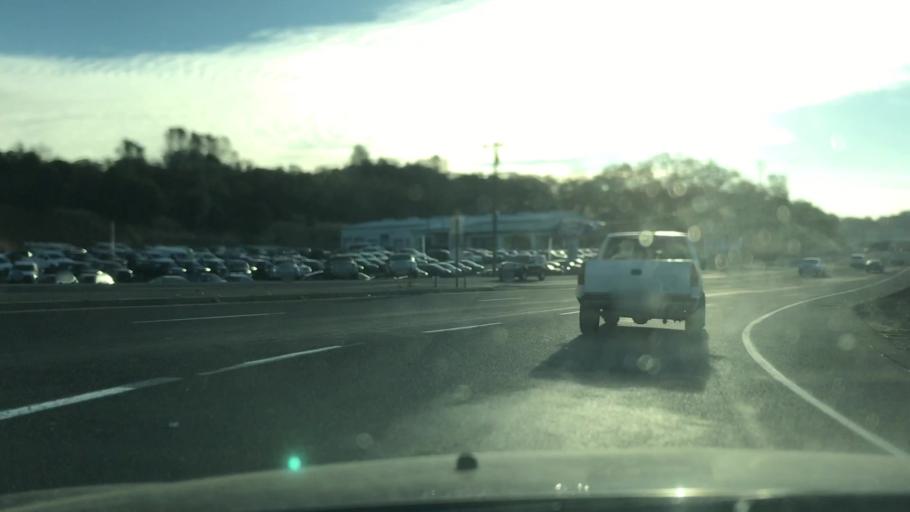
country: US
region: California
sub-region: Tuolumne County
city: East Sonora
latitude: 37.9760
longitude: -120.3562
